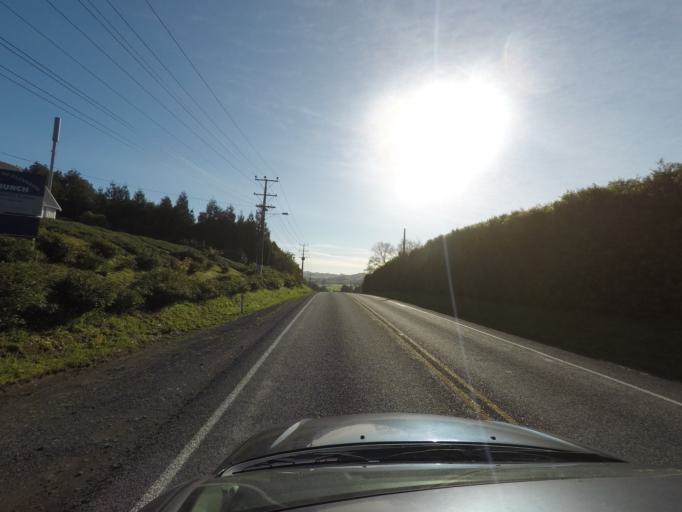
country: NZ
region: Auckland
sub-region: Auckland
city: Red Hill
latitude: -37.0135
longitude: 174.9480
